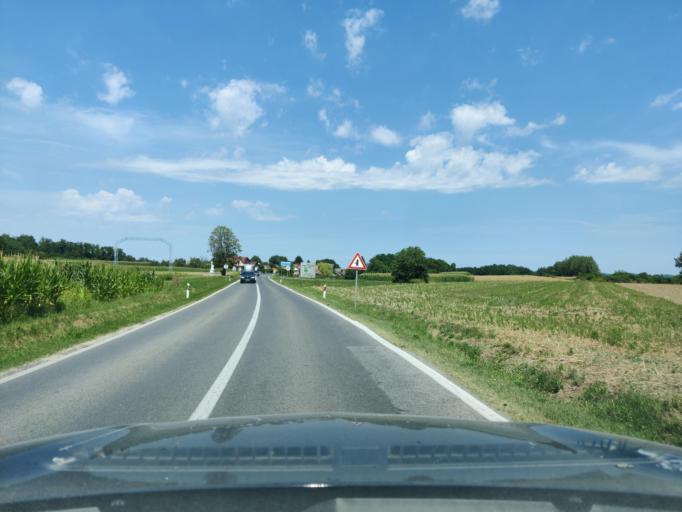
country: HR
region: Medimurska
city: Vratisinec
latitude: 46.4651
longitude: 16.4259
